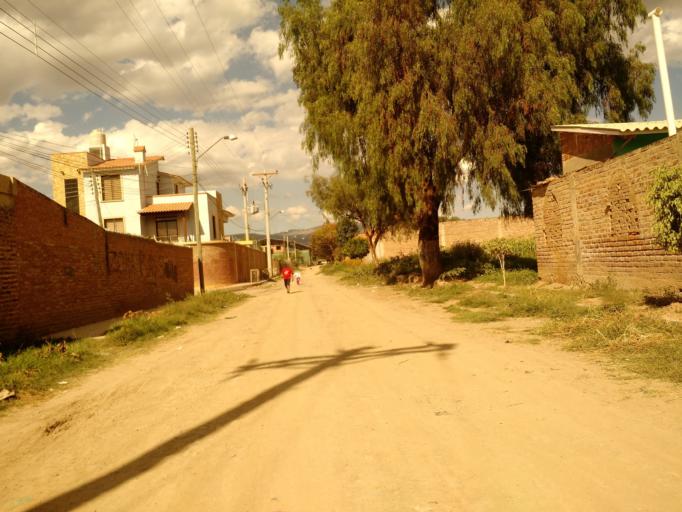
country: BO
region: Cochabamba
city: Cochabamba
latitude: -17.4581
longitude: -66.1570
